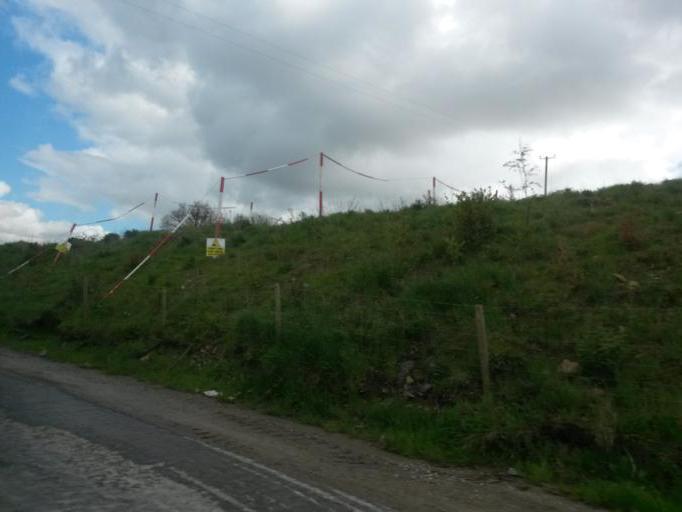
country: IE
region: Leinster
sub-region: Loch Garman
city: Enniscorthy
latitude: 52.4427
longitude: -6.5408
